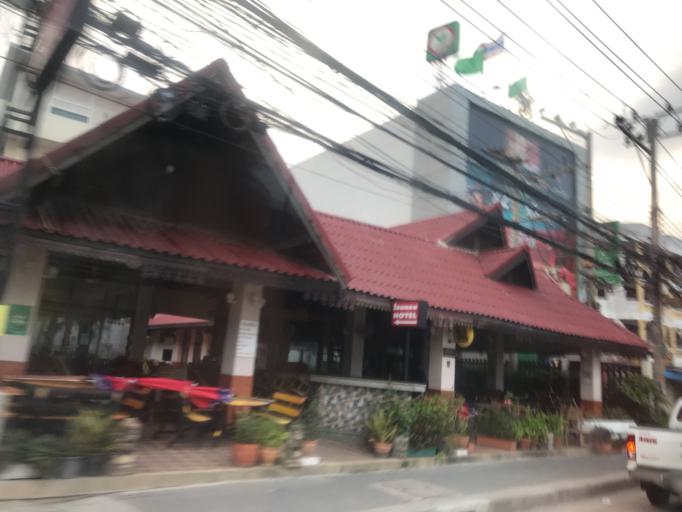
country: TH
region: Chon Buri
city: Phatthaya
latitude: 12.8976
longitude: 100.8680
